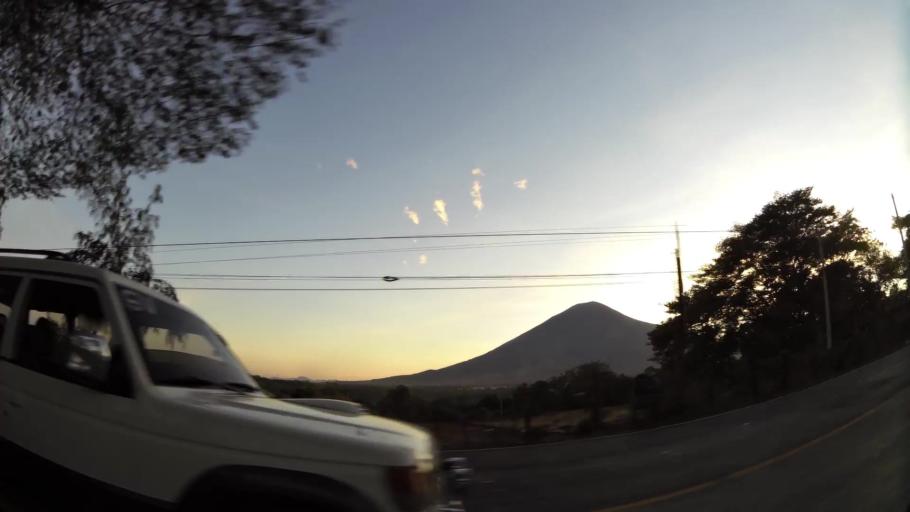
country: SV
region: San Miguel
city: San Miguel
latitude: 13.5006
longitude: -88.2144
